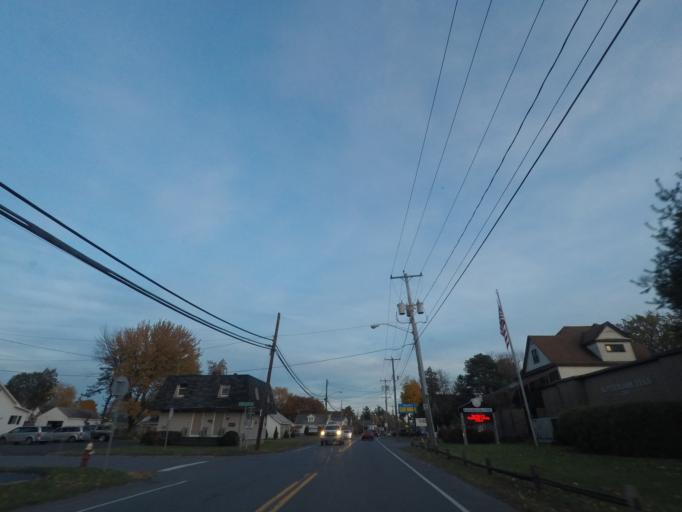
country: US
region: New York
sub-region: Schenectady County
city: Rotterdam
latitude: 42.7859
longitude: -73.9682
